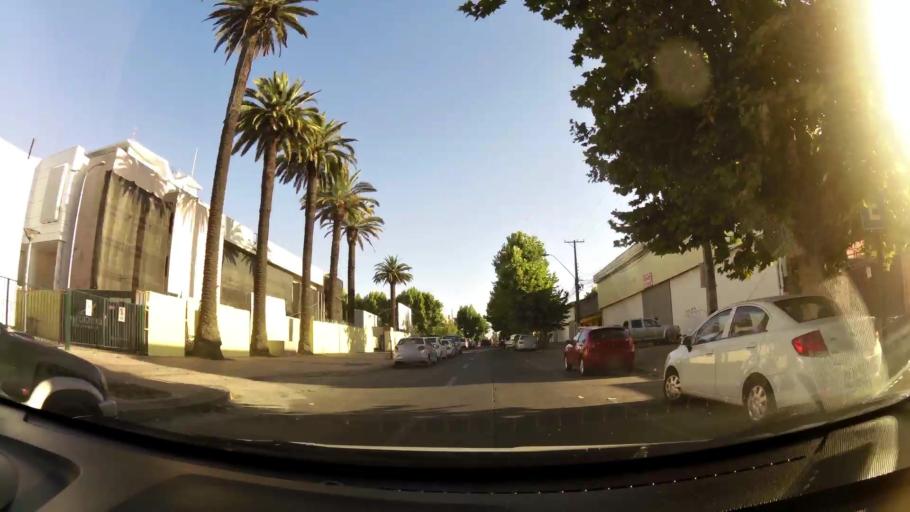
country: CL
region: Maule
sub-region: Provincia de Talca
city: Talca
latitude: -35.4266
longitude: -71.6478
